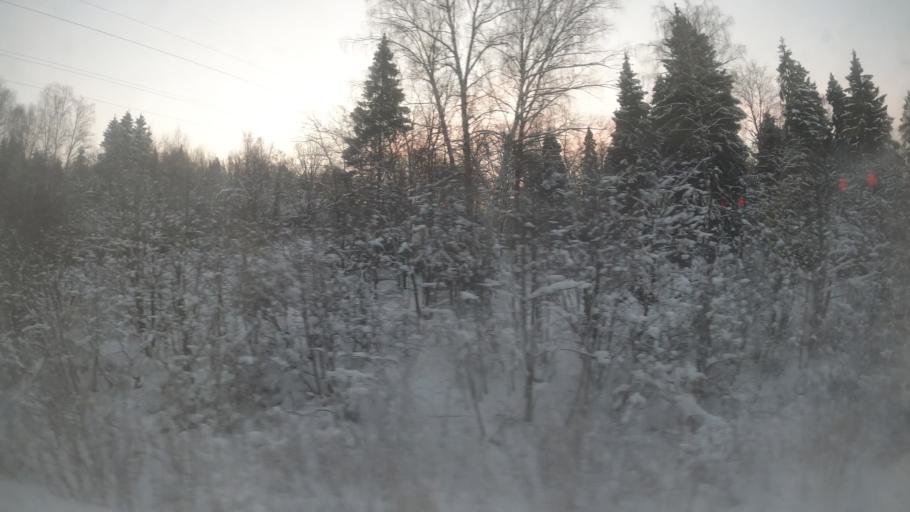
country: RU
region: Moskovskaya
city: Lugovaya
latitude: 56.0634
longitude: 37.4908
